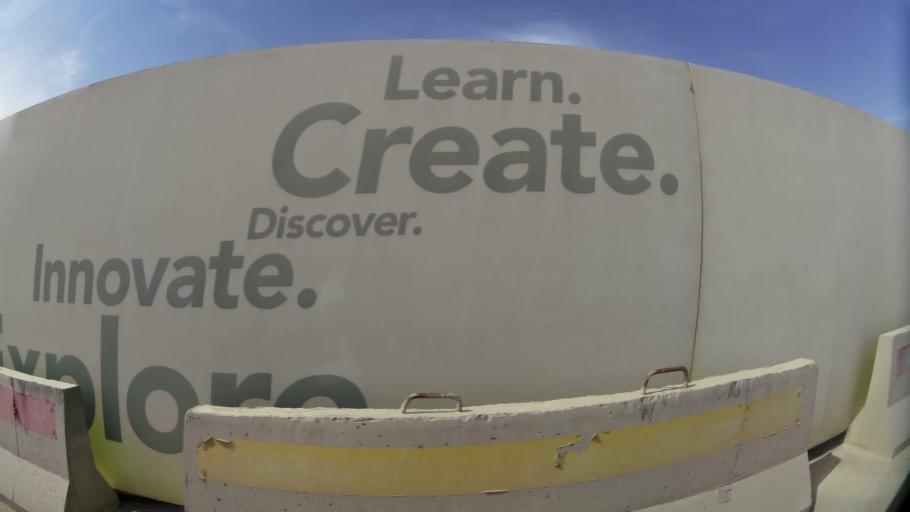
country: QA
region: Baladiyat ar Rayyan
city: Ar Rayyan
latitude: 25.3209
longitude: 51.4269
